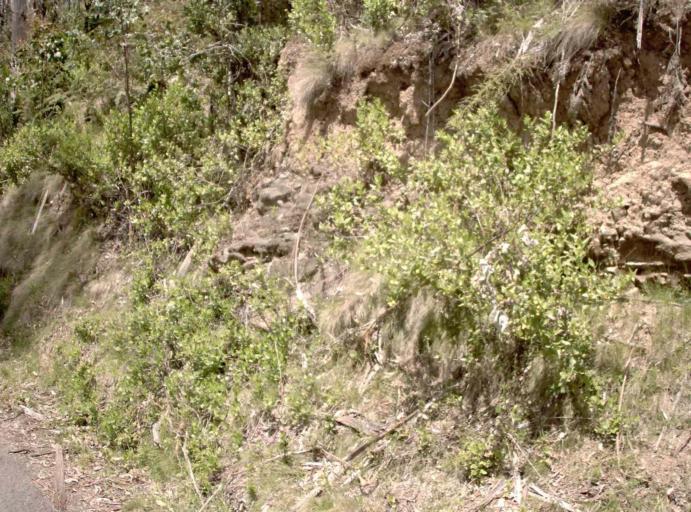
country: AU
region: Victoria
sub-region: Latrobe
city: Traralgon
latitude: -38.4308
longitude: 146.5288
